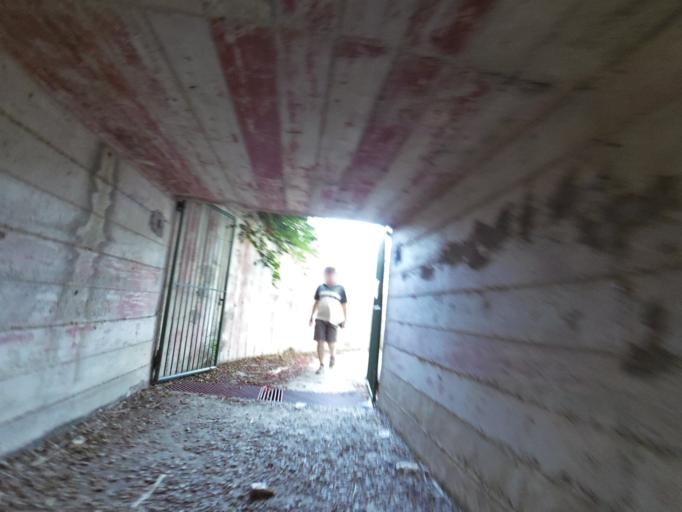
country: IT
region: Calabria
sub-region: Provincia di Reggio Calabria
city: Monasterace Marina
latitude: 38.4509
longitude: 16.5792
